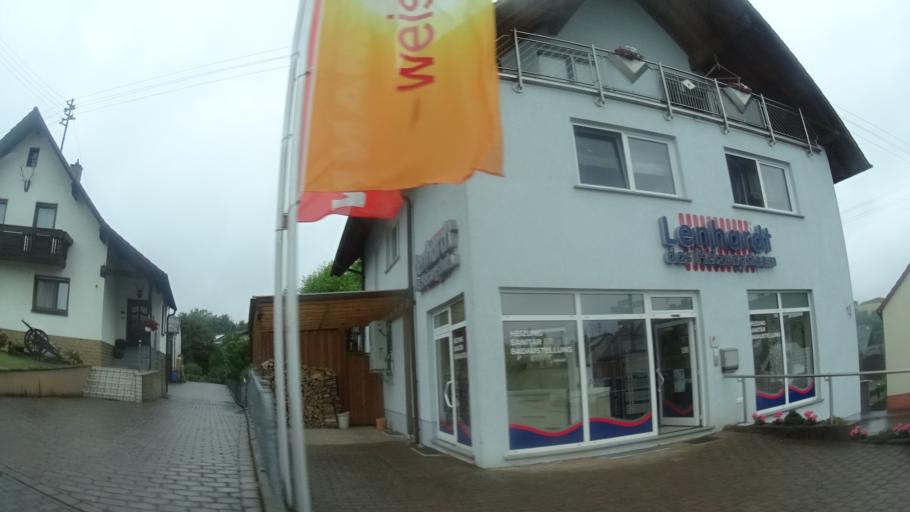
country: DE
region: Rheinland-Pfalz
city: Gries
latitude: 49.4176
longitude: 7.4272
